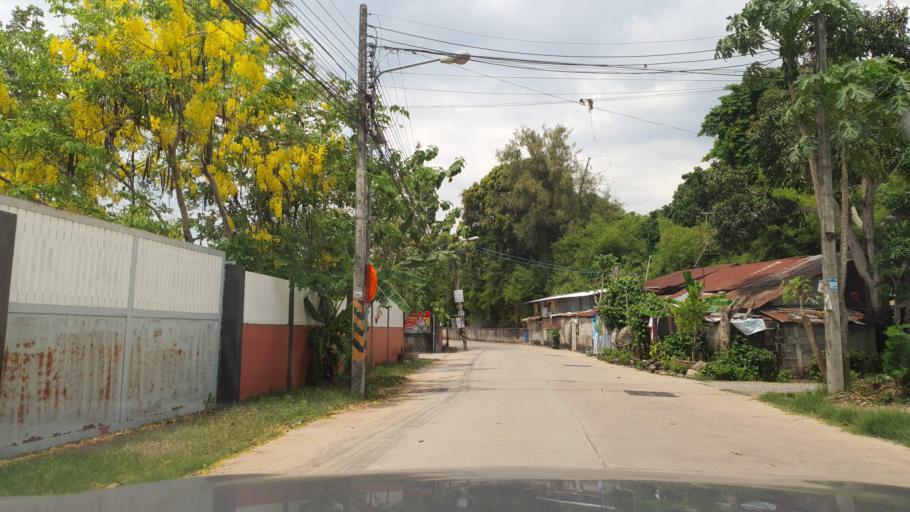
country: TH
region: Chon Buri
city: Phatthaya
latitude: 12.8870
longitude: 100.8928
